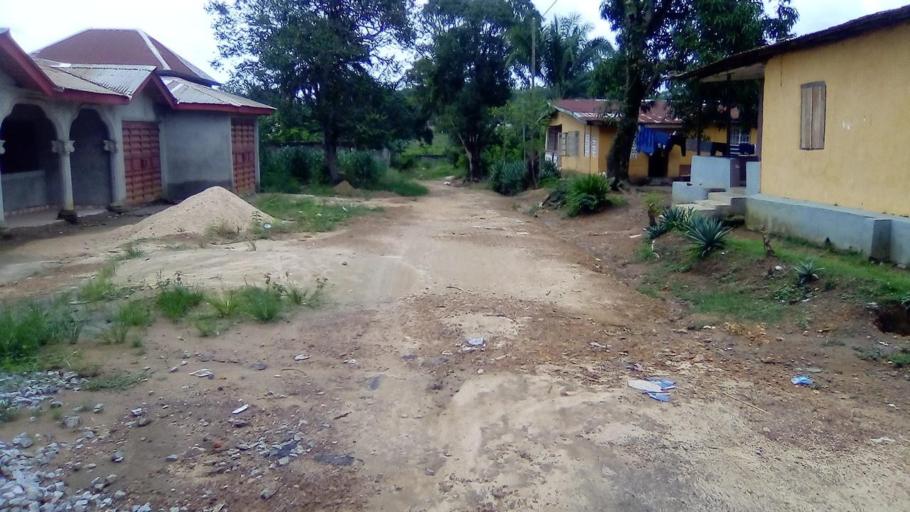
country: SL
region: Southern Province
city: Bo
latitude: 7.9509
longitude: -11.7513
